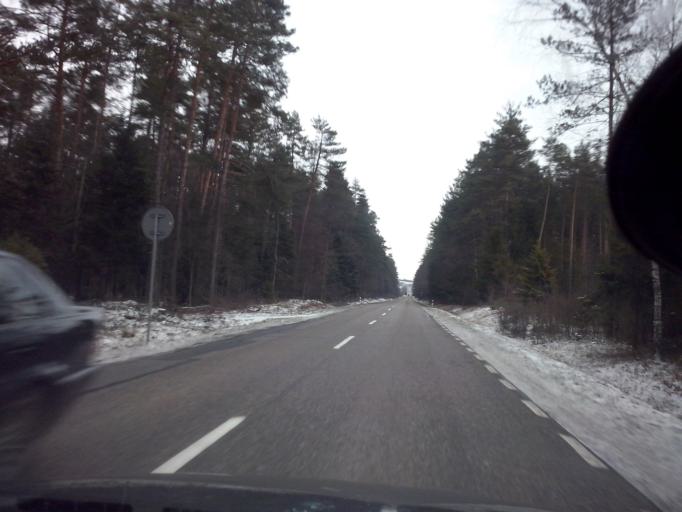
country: PL
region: Lublin Voivodeship
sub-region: Powiat bilgorajski
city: Tereszpol
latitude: 50.5944
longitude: 22.8617
